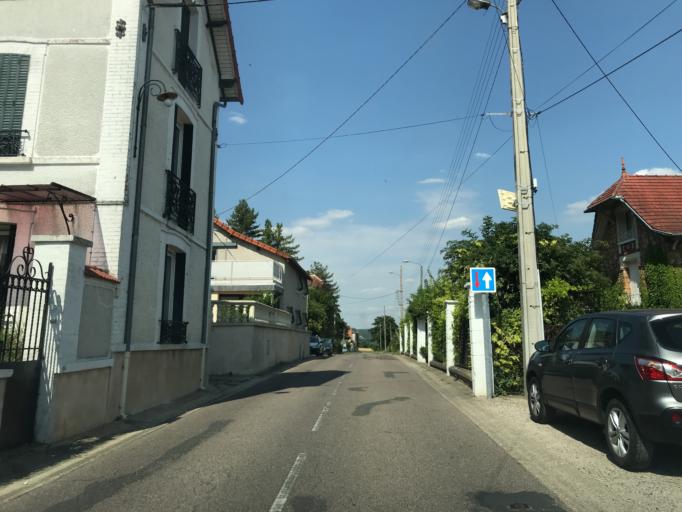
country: FR
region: Ile-de-France
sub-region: Departement des Yvelines
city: Freneuse
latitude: 49.0529
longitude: 1.5917
